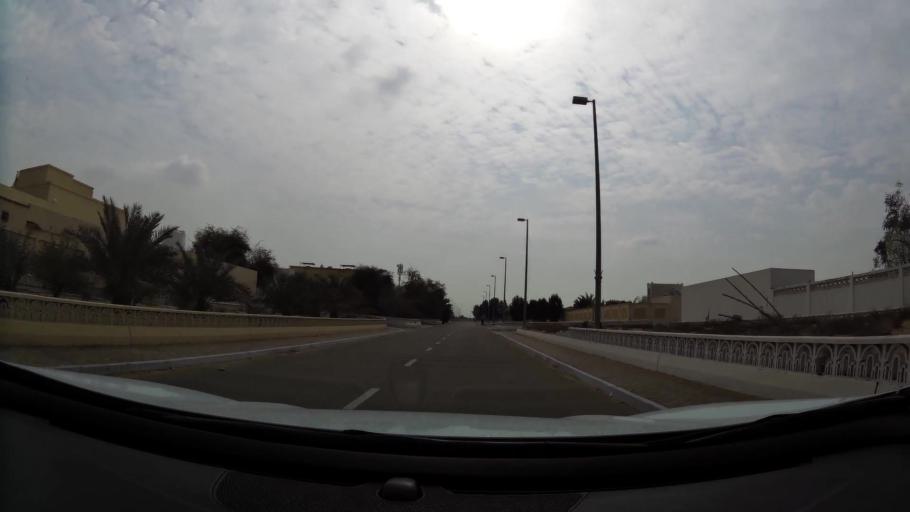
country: AE
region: Abu Dhabi
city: Abu Dhabi
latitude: 24.6480
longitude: 54.7311
